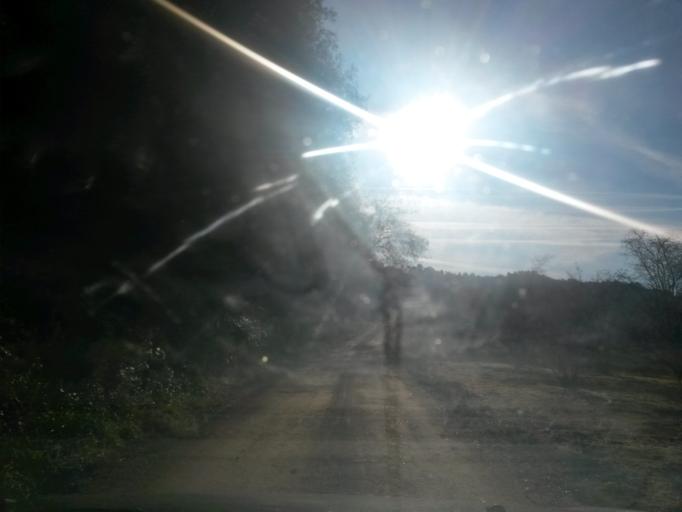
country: ES
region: Catalonia
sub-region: Provincia de Girona
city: la Cellera de Ter
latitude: 41.9831
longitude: 2.6276
